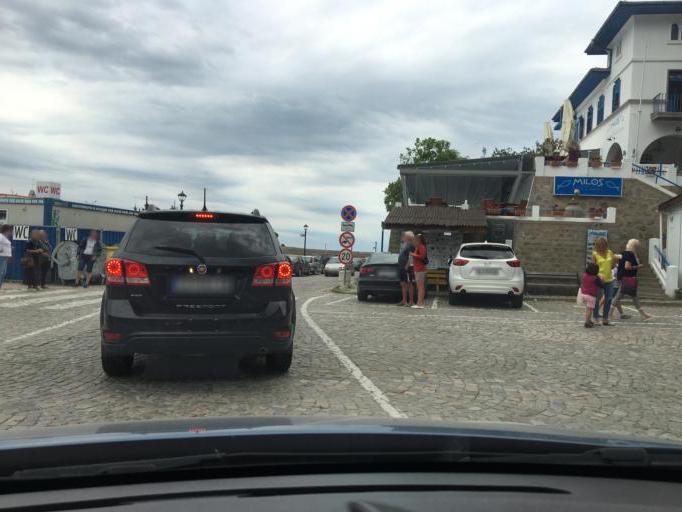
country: BG
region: Burgas
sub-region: Obshtina Sozopol
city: Sozopol
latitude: 42.4218
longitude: 27.6920
